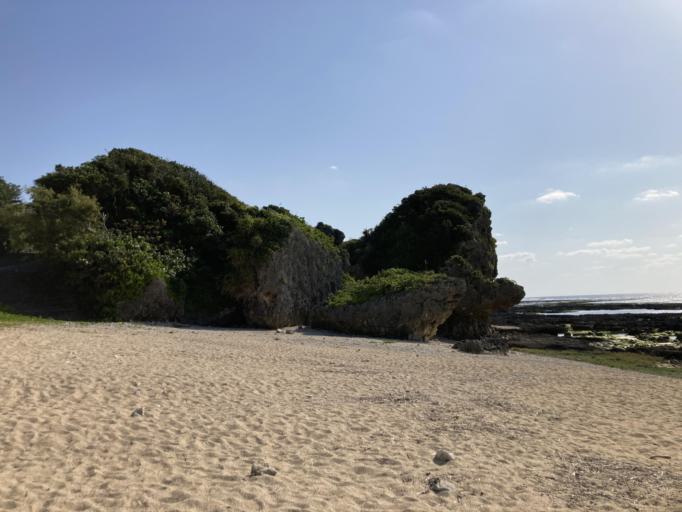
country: JP
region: Okinawa
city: Itoman
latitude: 26.1191
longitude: 127.7480
